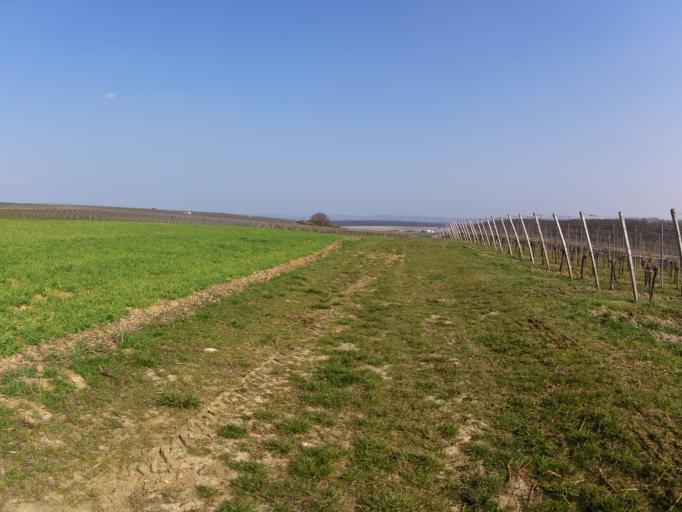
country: DE
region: Bavaria
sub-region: Regierungsbezirk Unterfranken
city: Mainstockheim
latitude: 49.7870
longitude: 10.1342
